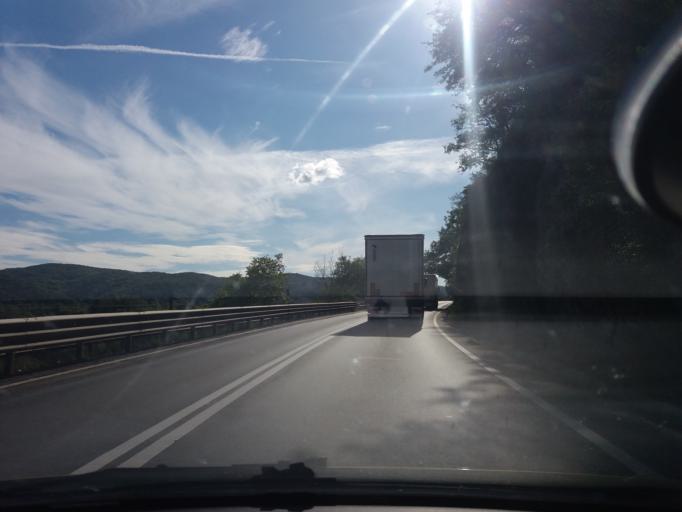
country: RO
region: Arad
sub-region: Comuna Savarsin
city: Savarsin
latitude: 46.0010
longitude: 22.3118
